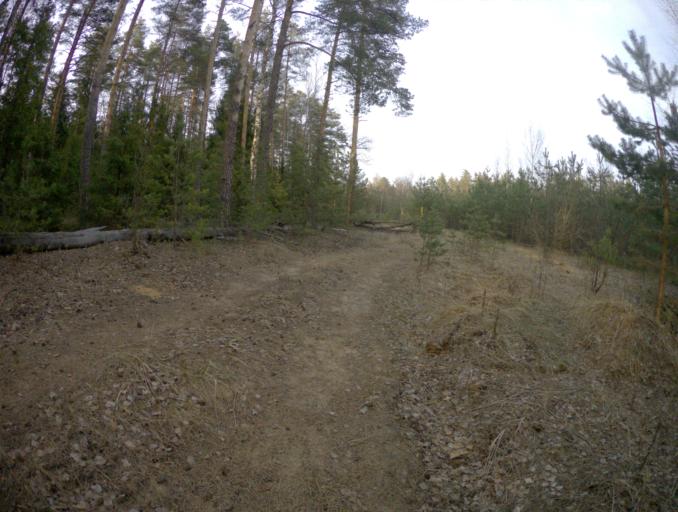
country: RU
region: Vladimir
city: Kommunar
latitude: 56.0710
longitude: 40.5084
